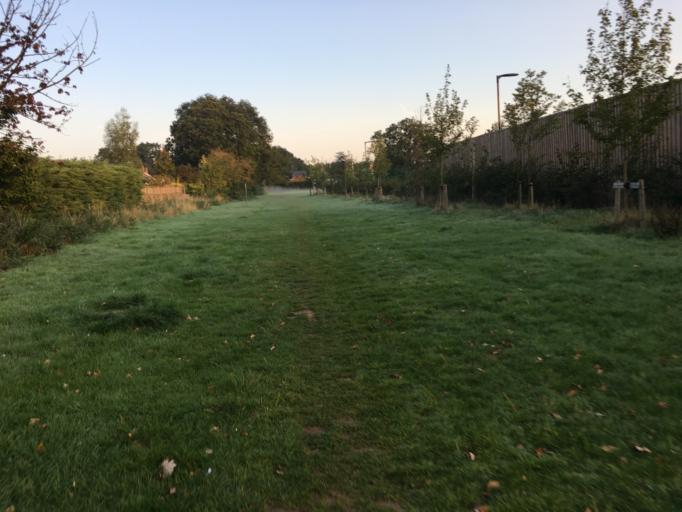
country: GB
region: England
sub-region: Warwickshire
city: Rugby
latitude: 52.3557
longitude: -1.2640
